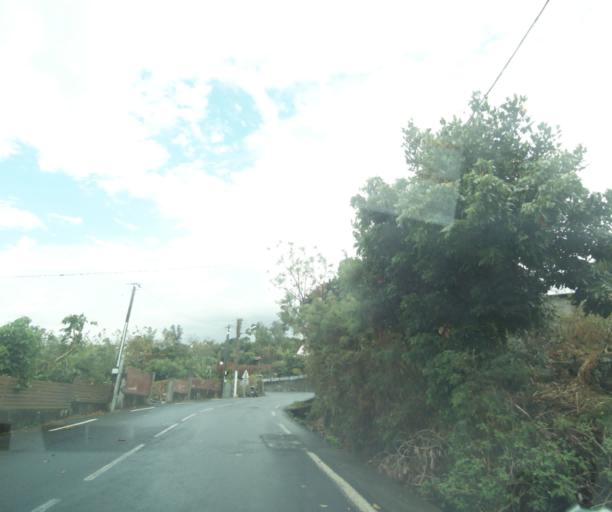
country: RE
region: Reunion
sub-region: Reunion
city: Saint-Paul
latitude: -21.0248
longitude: 55.2864
